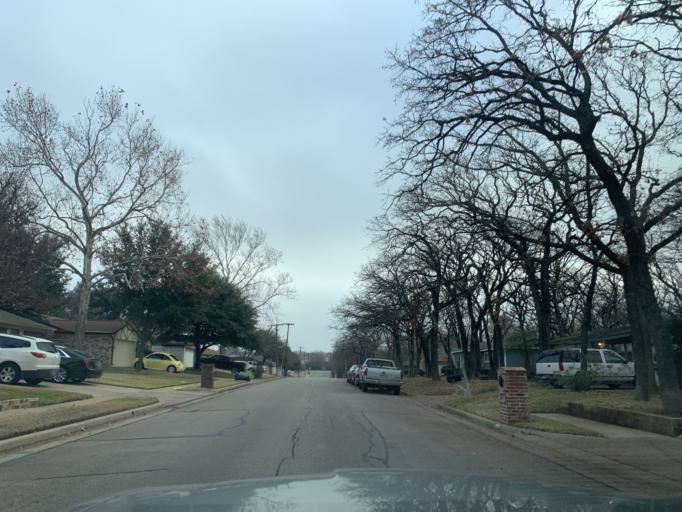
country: US
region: Texas
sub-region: Tarrant County
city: Bedford
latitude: 32.8344
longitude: -97.1457
